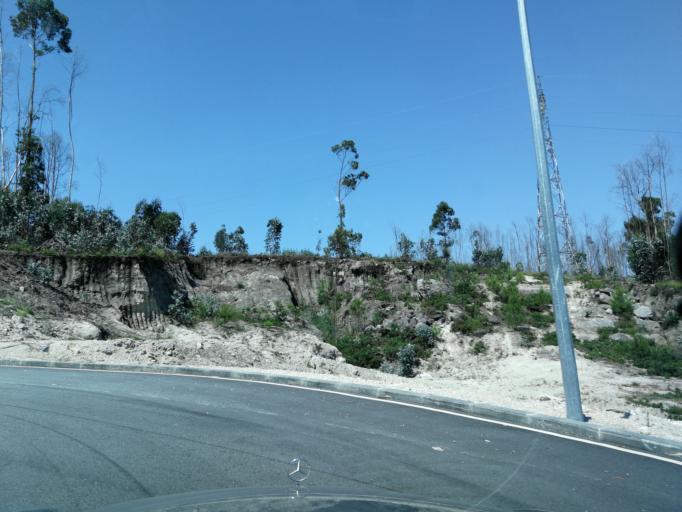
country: PT
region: Braga
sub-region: Braga
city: Adaufe
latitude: 41.5576
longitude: -8.3543
